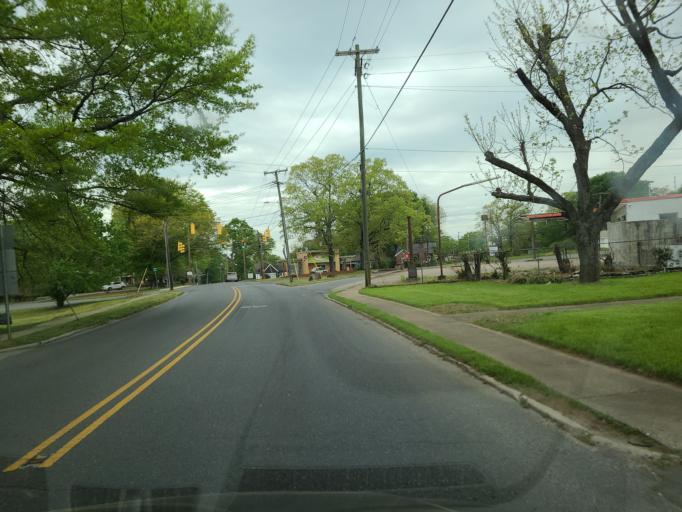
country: US
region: North Carolina
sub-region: Cleveland County
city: Shelby
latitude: 35.2952
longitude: -81.5265
